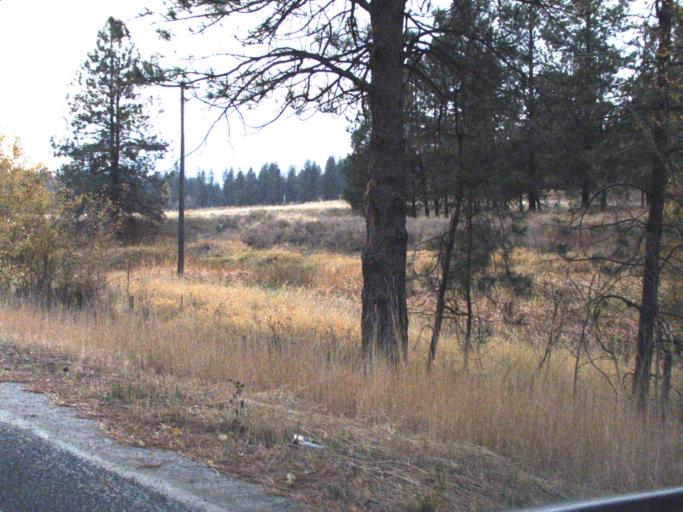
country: US
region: Washington
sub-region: Lincoln County
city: Davenport
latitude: 47.9838
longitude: -118.2920
